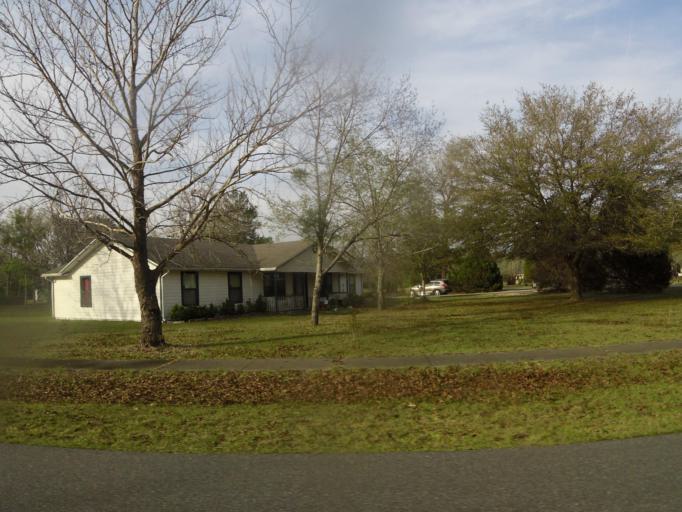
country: US
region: Florida
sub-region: Clay County
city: Middleburg
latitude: 30.1149
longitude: -81.8874
